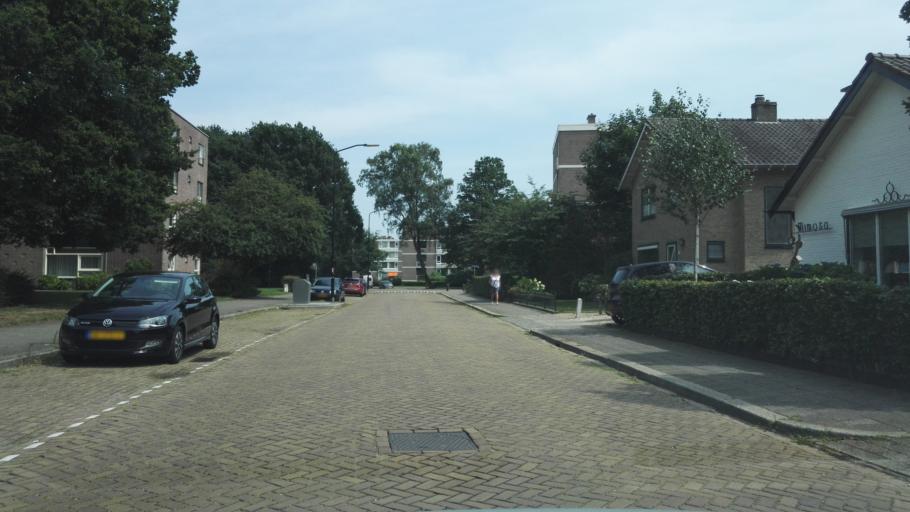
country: NL
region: Gelderland
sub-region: Gemeente Apeldoorn
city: Apeldoorn
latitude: 52.2042
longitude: 5.9328
